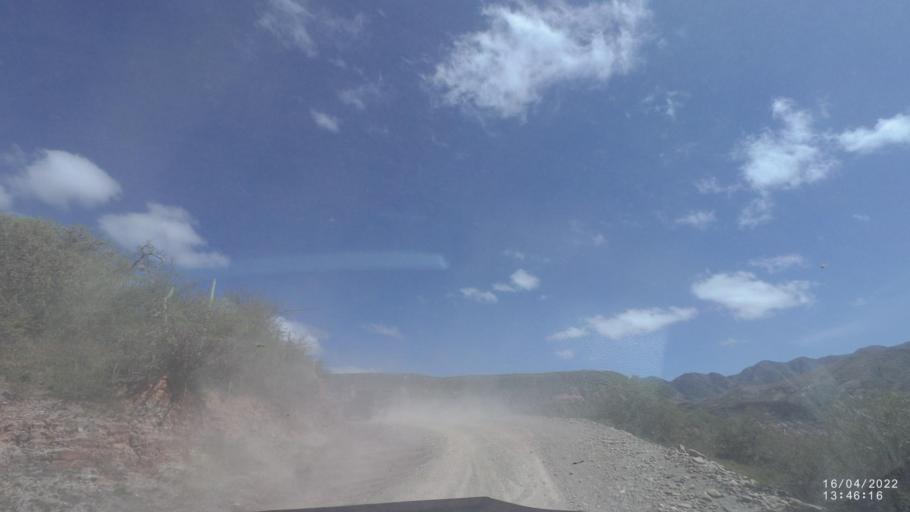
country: BO
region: Cochabamba
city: Mizque
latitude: -18.0050
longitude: -65.5888
